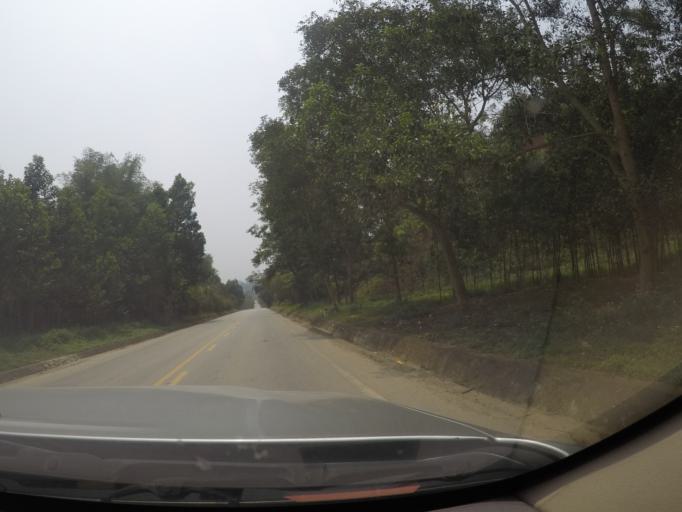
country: VN
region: Thanh Hoa
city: Thi Tran Thuong Xuan
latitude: 19.8600
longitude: 105.4093
